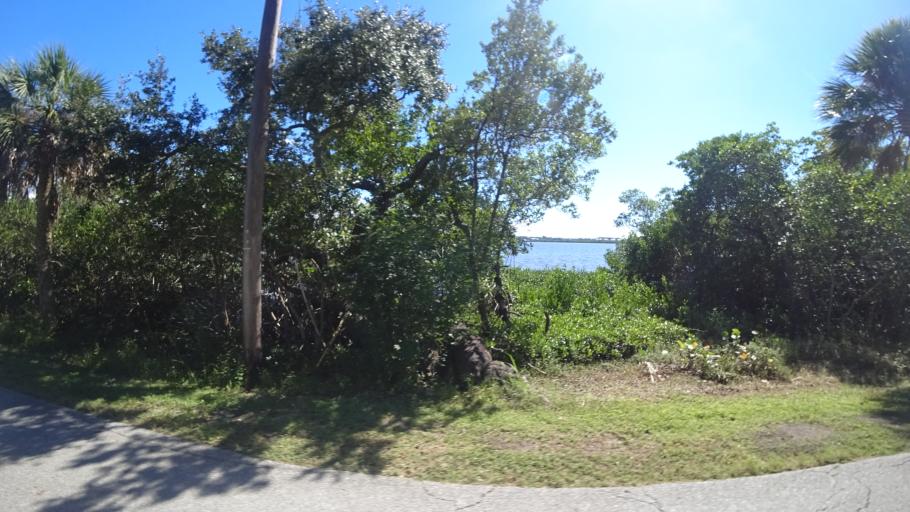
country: US
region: Florida
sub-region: Manatee County
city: Memphis
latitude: 27.5753
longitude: -82.5681
